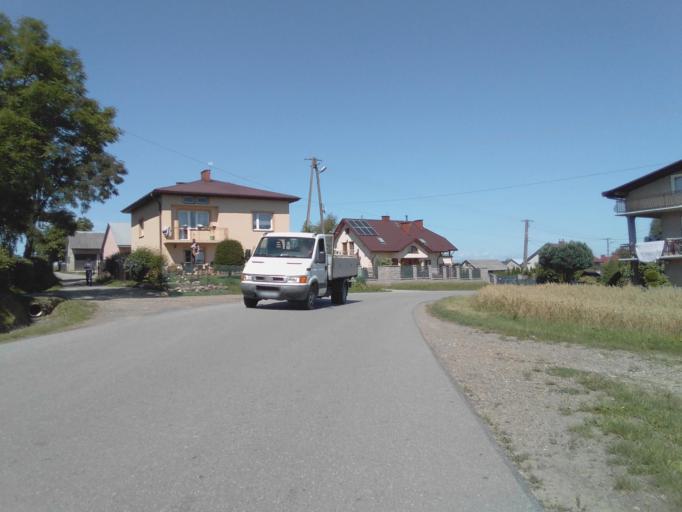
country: PL
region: Subcarpathian Voivodeship
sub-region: Powiat krosnienski
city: Chorkowka
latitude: 49.6431
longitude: 21.6089
